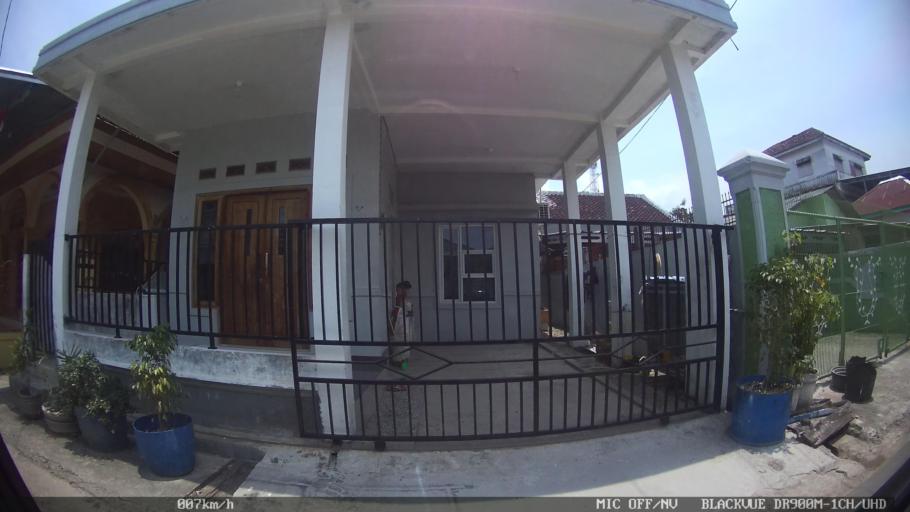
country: ID
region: Lampung
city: Bandarlampung
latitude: -5.4554
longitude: 105.2624
